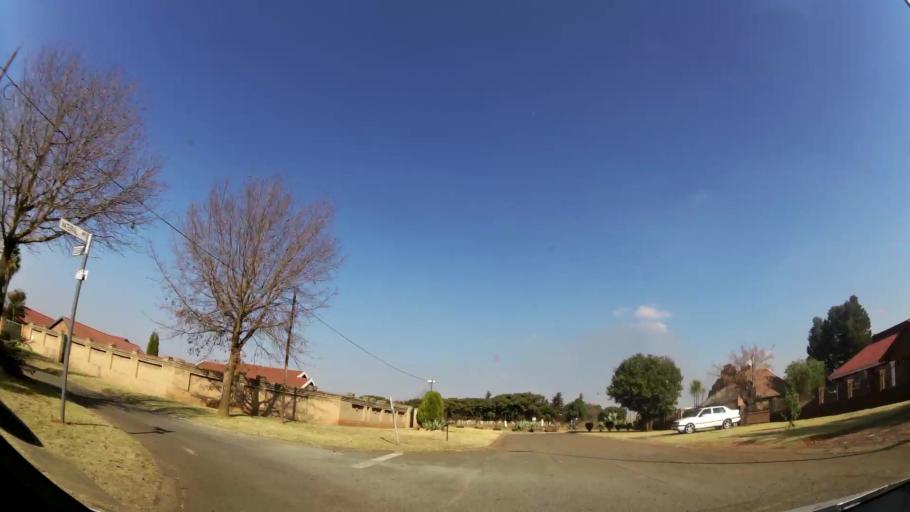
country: ZA
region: Gauteng
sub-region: Ekurhuleni Metropolitan Municipality
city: Brakpan
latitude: -26.2342
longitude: 28.3341
